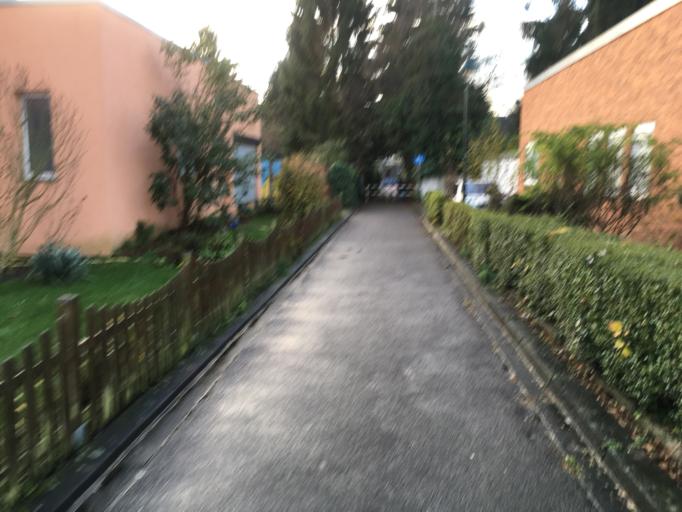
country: DE
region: North Rhine-Westphalia
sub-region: Regierungsbezirk Dusseldorf
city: Erkrath
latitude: 51.2391
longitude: 6.8558
